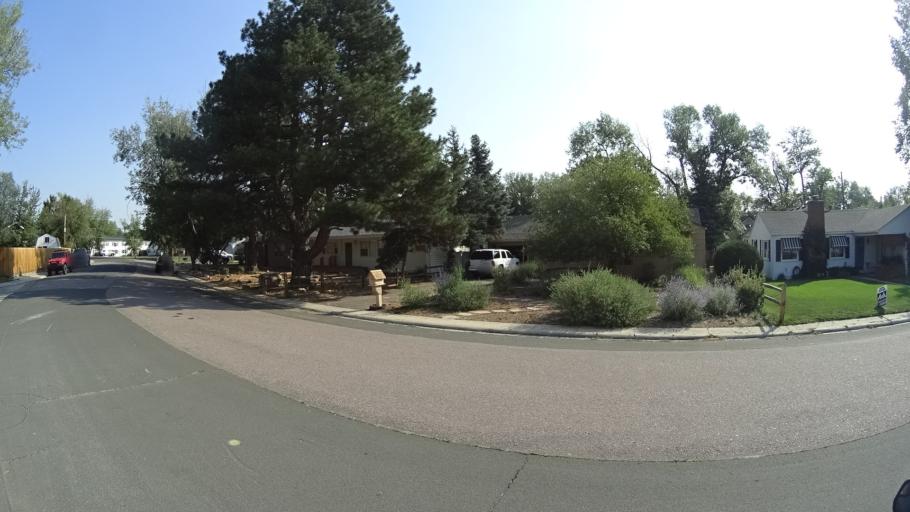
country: US
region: Colorado
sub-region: El Paso County
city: Colorado Springs
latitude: 38.8039
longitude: -104.8369
